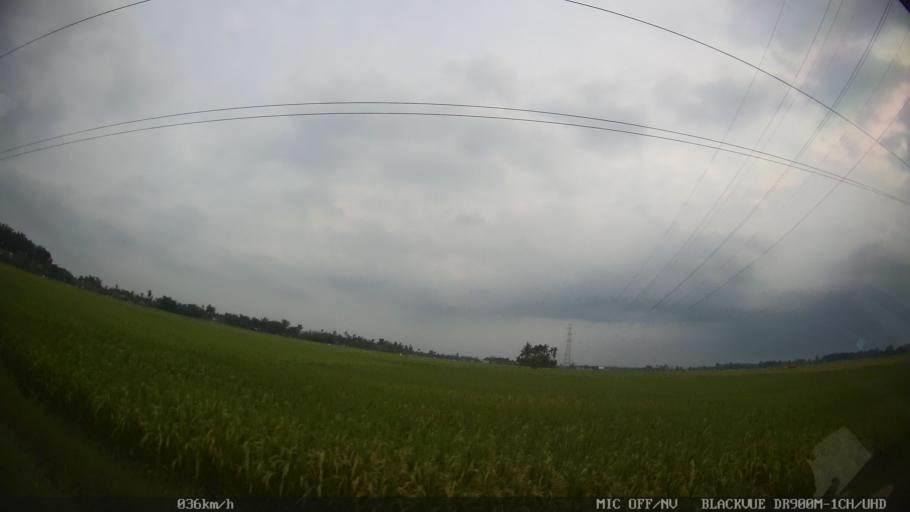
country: ID
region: North Sumatra
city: Sunggal
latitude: 3.5614
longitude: 98.5930
